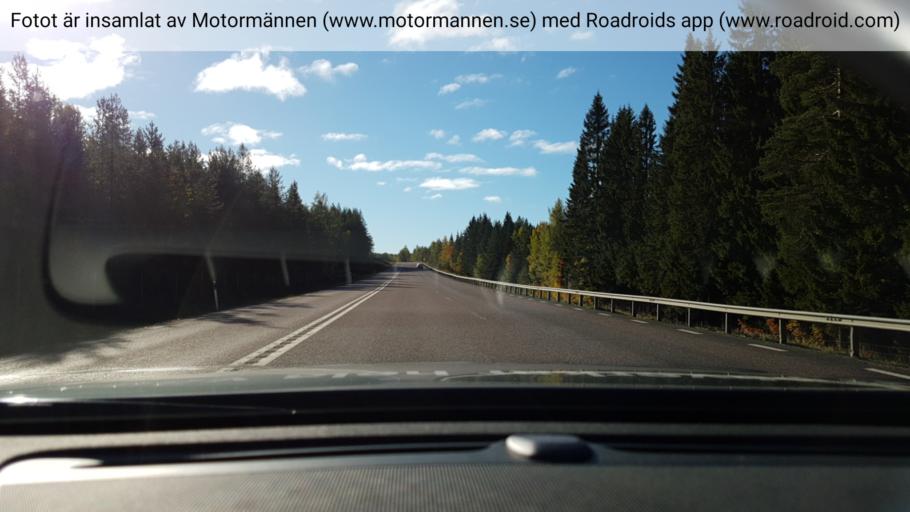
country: SE
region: Vaesterbotten
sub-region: Skelleftea Kommun
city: Burea
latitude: 64.4494
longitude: 21.2838
